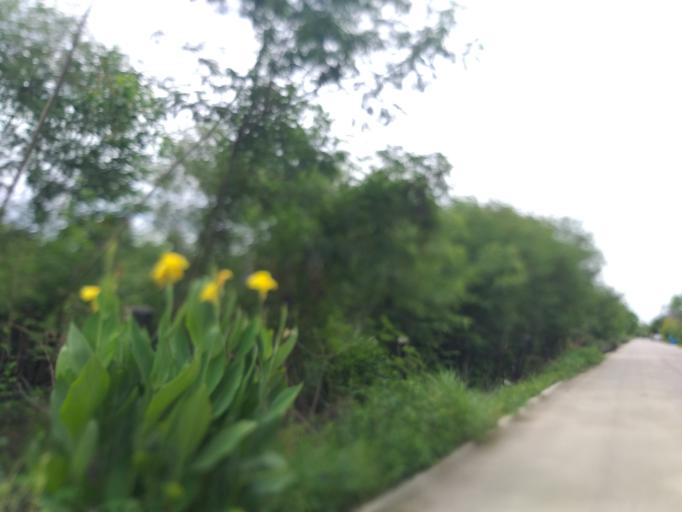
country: TH
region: Pathum Thani
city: Ban Lam Luk Ka
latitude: 14.0033
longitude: 100.8660
